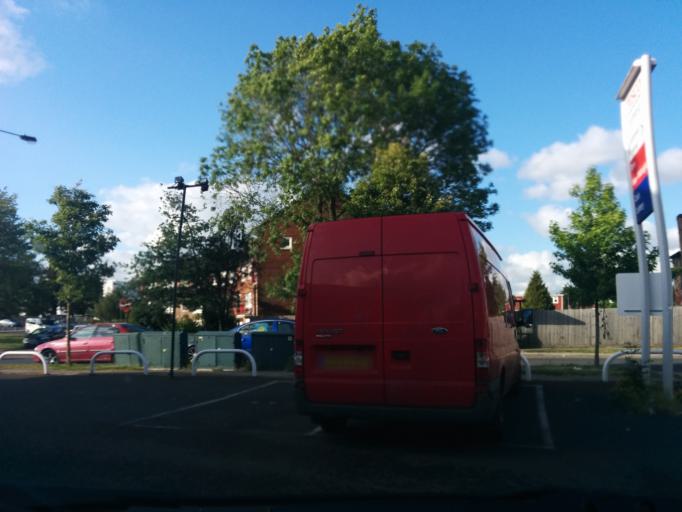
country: GB
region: England
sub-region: Greater London
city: Greenhill
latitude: 51.5716
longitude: -0.3535
